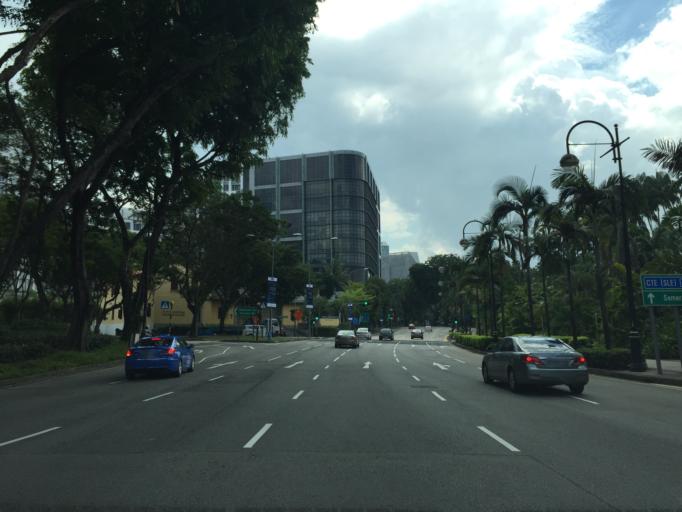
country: SG
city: Singapore
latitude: 1.2986
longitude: 103.8444
